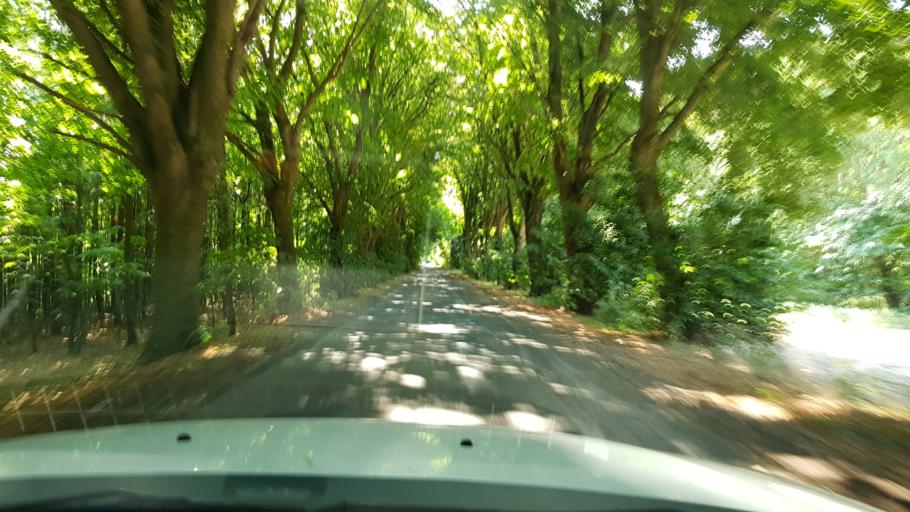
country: PL
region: West Pomeranian Voivodeship
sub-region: Powiat gryfinski
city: Chojna
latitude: 52.9427
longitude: 14.5131
